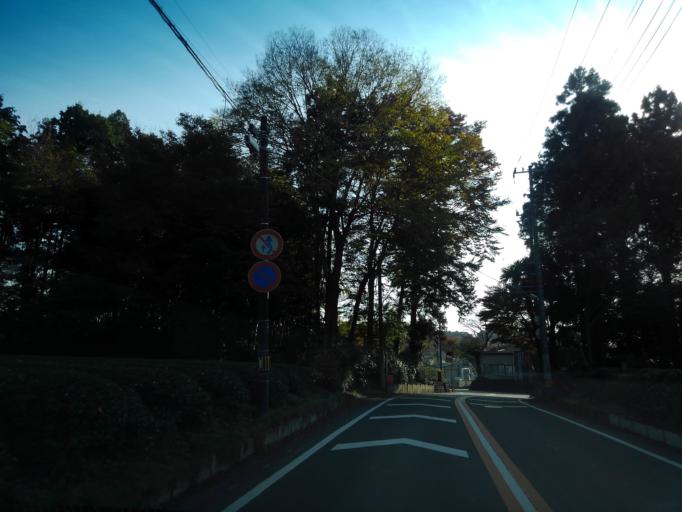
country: JP
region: Saitama
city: Tokorozawa
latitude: 35.7917
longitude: 139.4185
